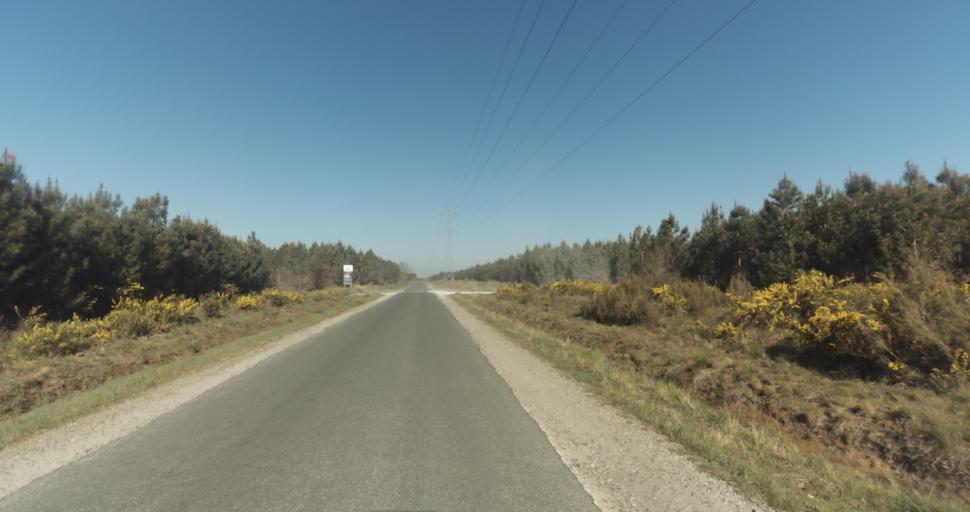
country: FR
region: Aquitaine
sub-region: Departement de la Gironde
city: Marcheprime
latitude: 44.7487
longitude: -0.8430
